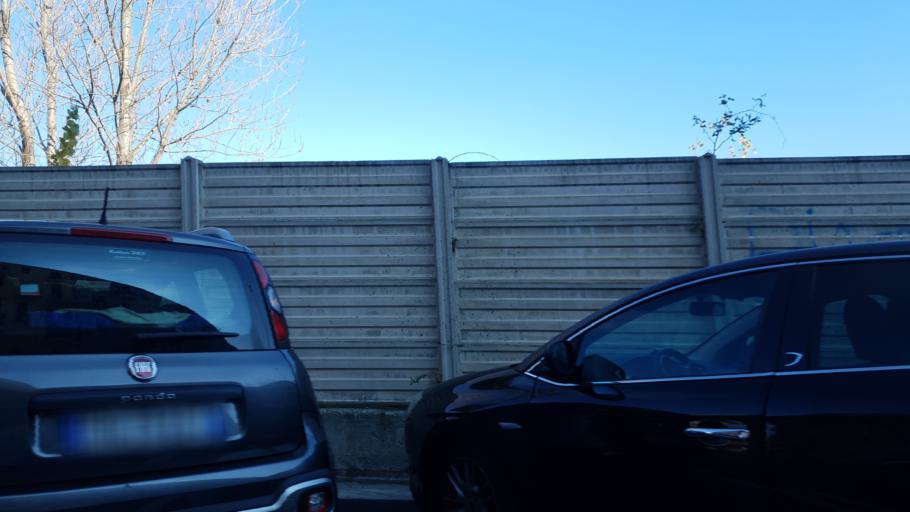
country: IT
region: Liguria
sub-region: Provincia di Savona
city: Vado Ligure
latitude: 44.2744
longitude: 8.4358
